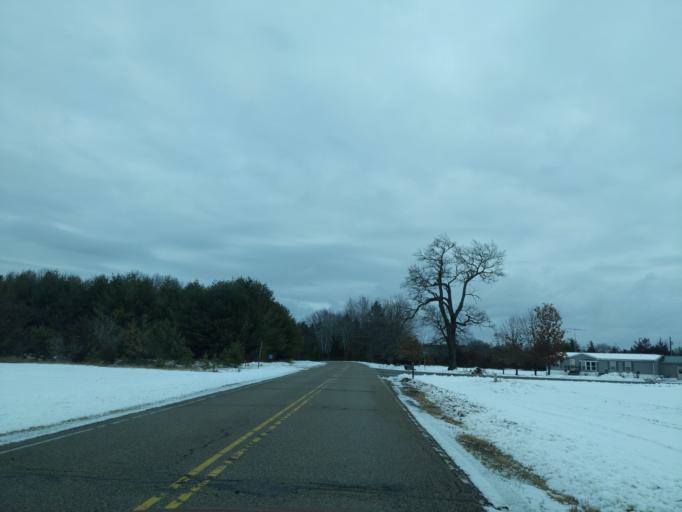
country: US
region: Wisconsin
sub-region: Marquette County
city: Westfield
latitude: 43.9089
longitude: -89.3710
